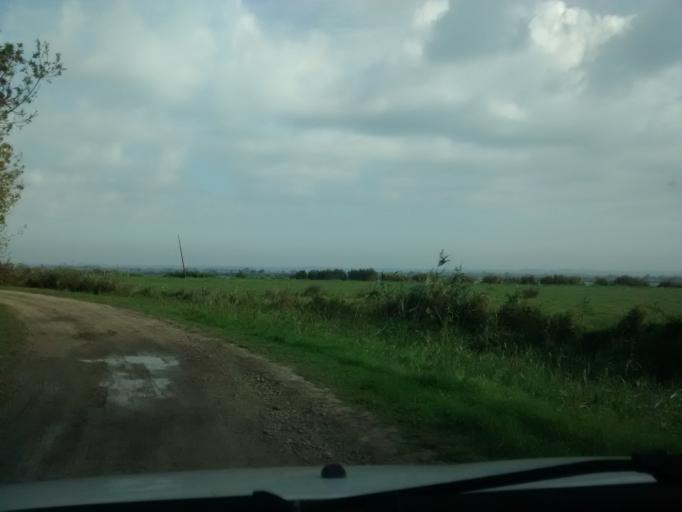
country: FR
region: Pays de la Loire
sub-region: Departement de la Loire-Atlantique
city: Cordemais
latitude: 47.2556
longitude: -1.8586
